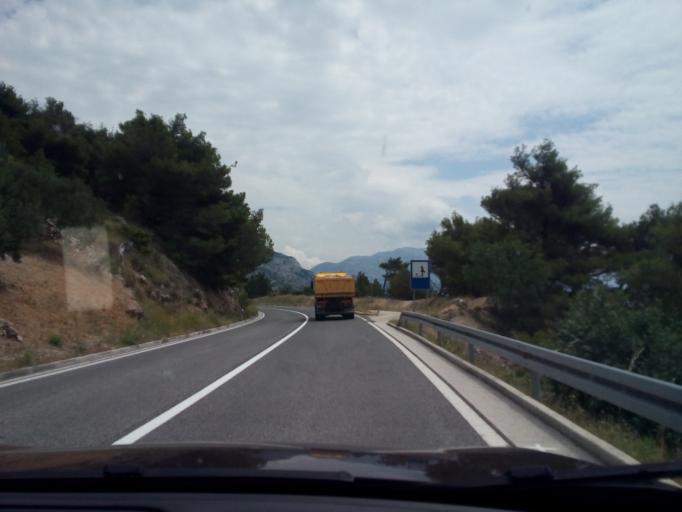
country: HR
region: Splitsko-Dalmatinska
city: Donja Brela
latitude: 43.4026
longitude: 16.8360
